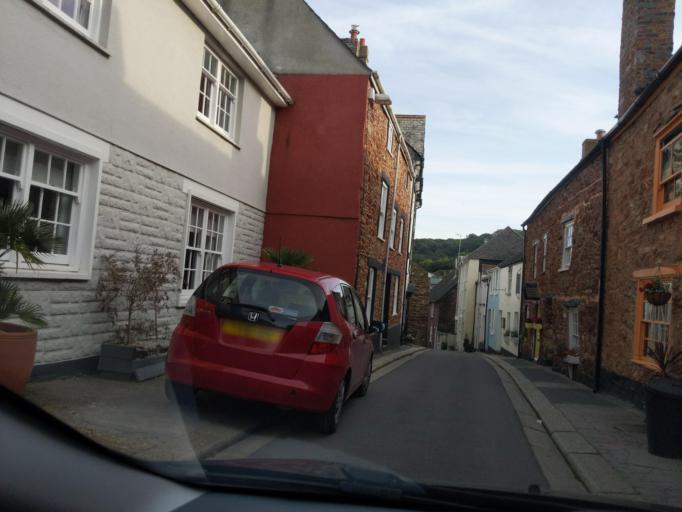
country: GB
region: England
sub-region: Cornwall
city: Millbrook
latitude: 50.3342
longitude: -4.2017
